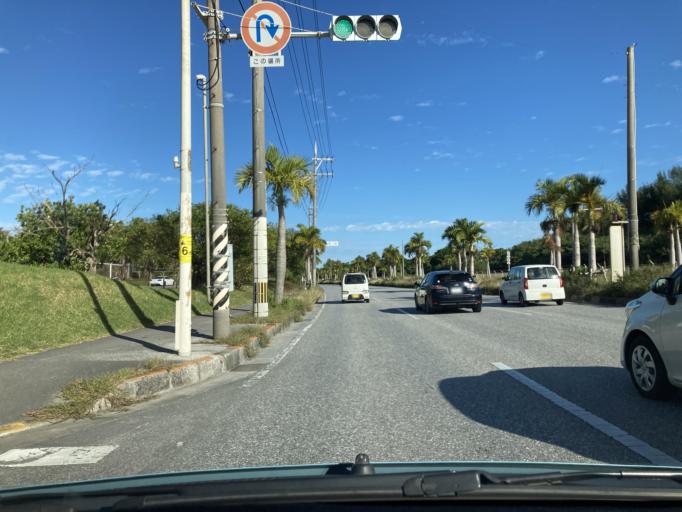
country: JP
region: Okinawa
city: Chatan
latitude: 26.3503
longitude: 127.7467
